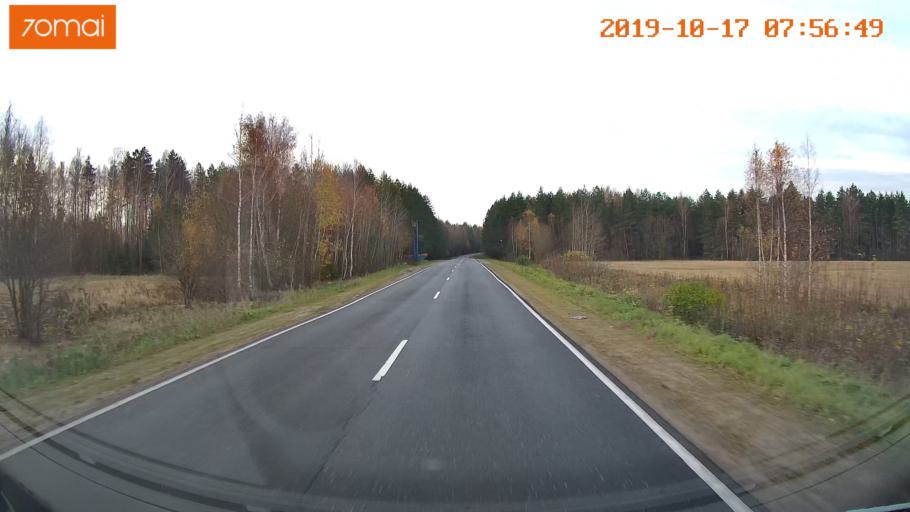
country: RU
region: Vladimir
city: Bavleny
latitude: 56.4184
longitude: 39.5858
